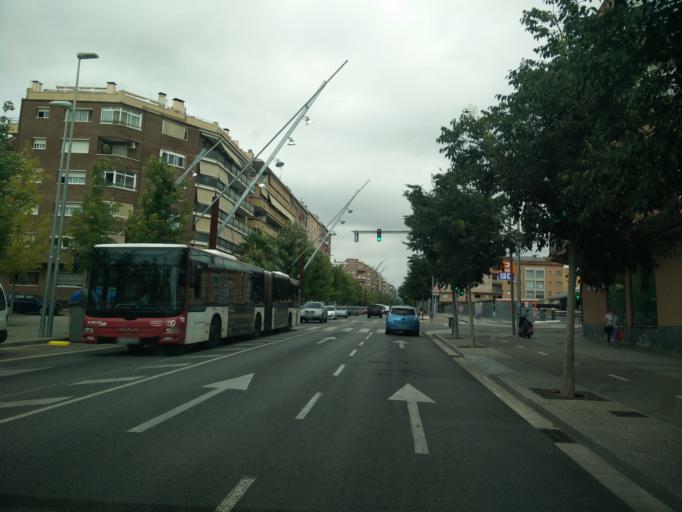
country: ES
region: Catalonia
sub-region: Provincia de Barcelona
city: Terrassa
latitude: 41.5600
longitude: 2.0283
